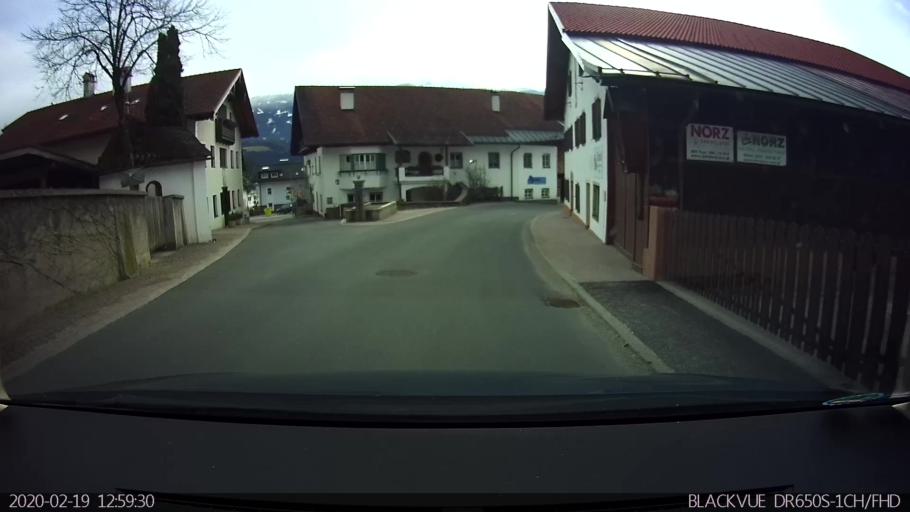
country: AT
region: Tyrol
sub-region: Politischer Bezirk Innsbruck Land
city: Thaur
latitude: 47.2920
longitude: 11.4718
